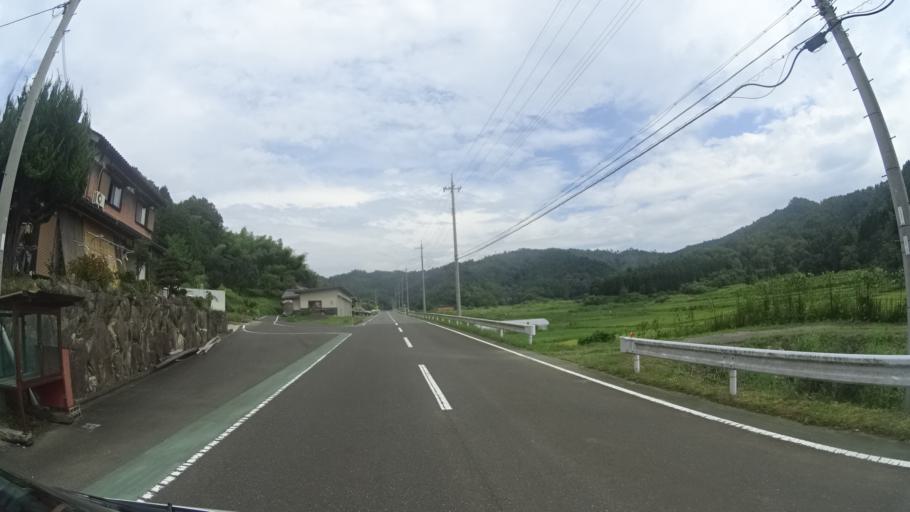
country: JP
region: Kyoto
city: Maizuru
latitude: 35.3564
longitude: 135.3268
